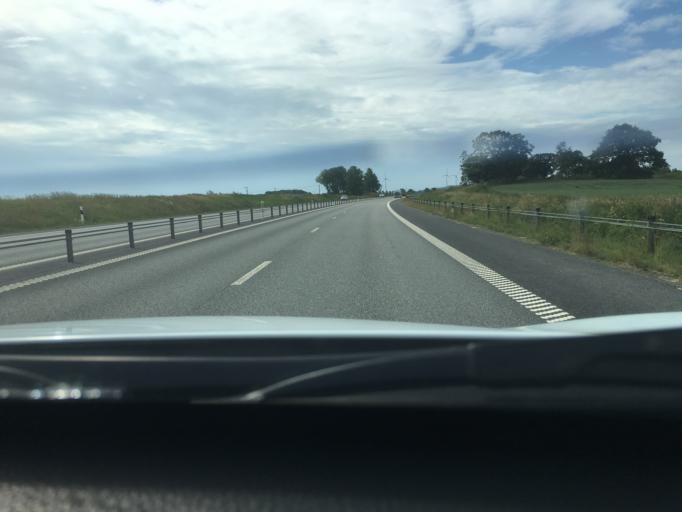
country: SE
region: Blekinge
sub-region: Solvesborgs Kommun
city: Soelvesborg
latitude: 56.0823
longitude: 14.6442
